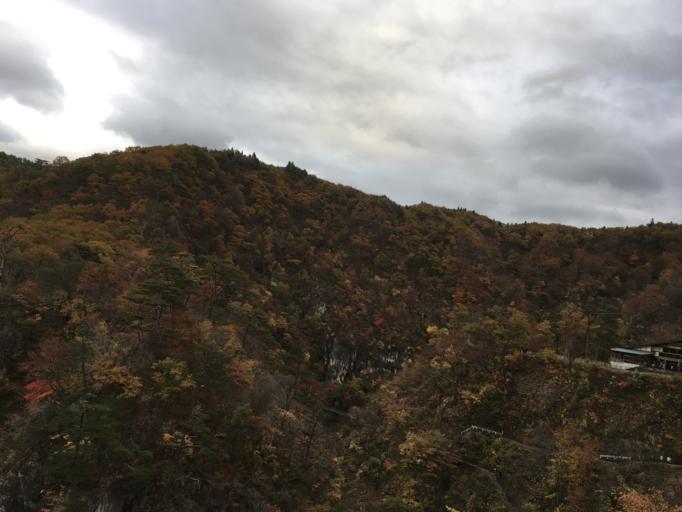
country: JP
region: Miyagi
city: Furukawa
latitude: 38.7301
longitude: 140.6893
